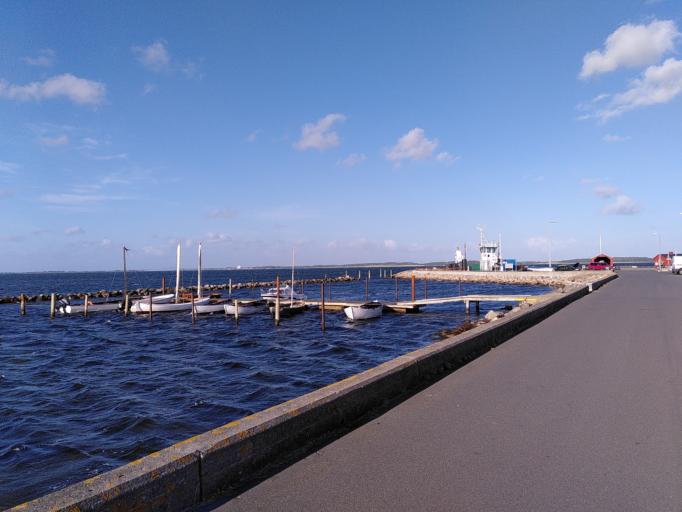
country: DK
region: South Denmark
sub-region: Langeland Kommune
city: Rudkobing
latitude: 54.9036
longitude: 10.6274
